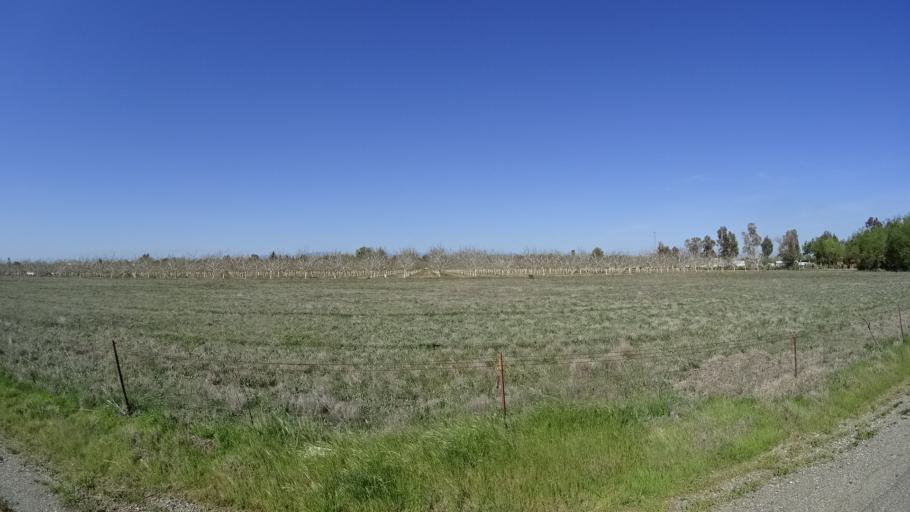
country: US
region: California
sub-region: Glenn County
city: Willows
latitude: 39.5360
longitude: -122.1886
